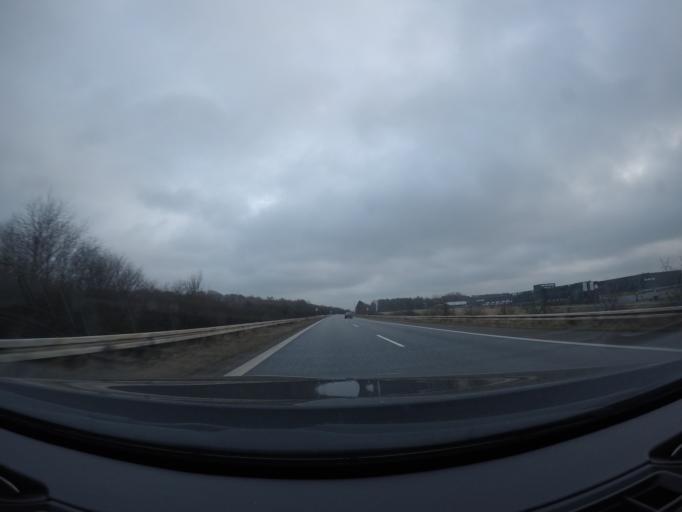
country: DK
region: South Denmark
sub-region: Fredericia Kommune
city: Taulov
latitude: 55.5390
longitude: 9.6630
